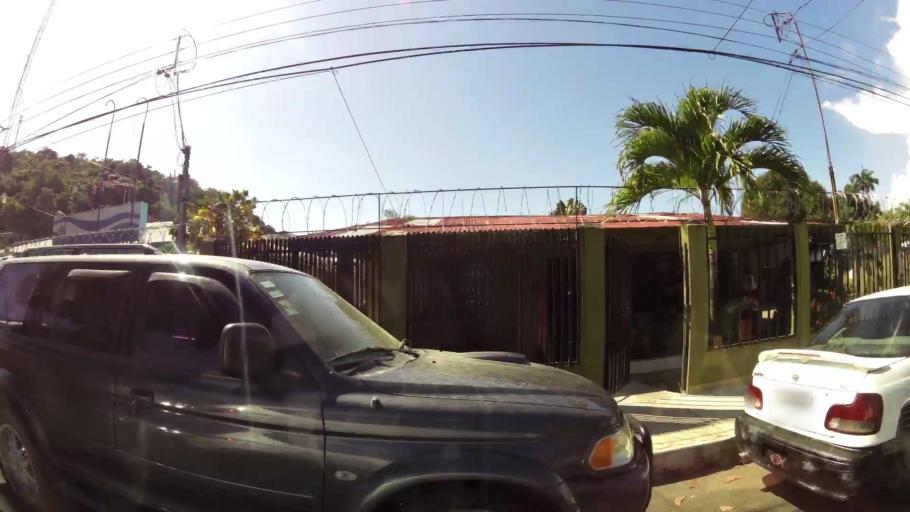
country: CR
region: Puntarenas
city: Quepos
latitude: 9.4306
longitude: -84.1612
